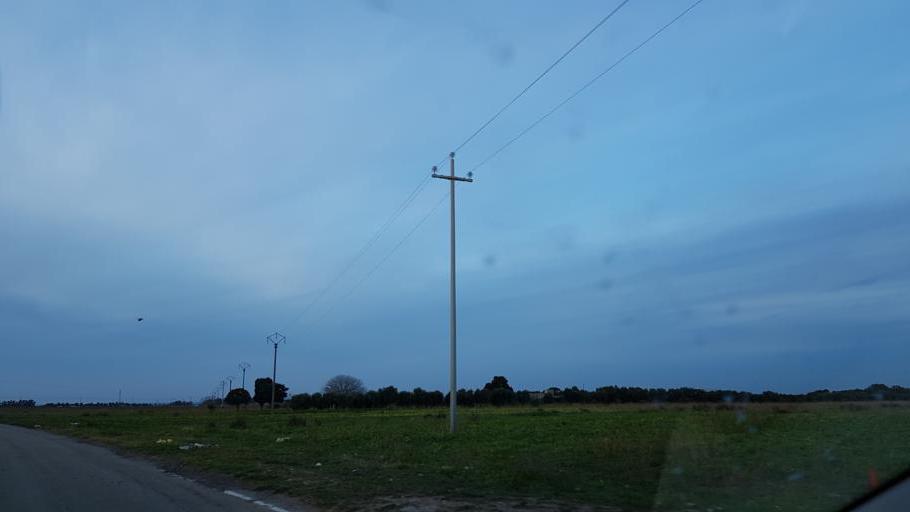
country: IT
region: Apulia
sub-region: Provincia di Brindisi
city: Brindisi
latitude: 40.6619
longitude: 17.9115
